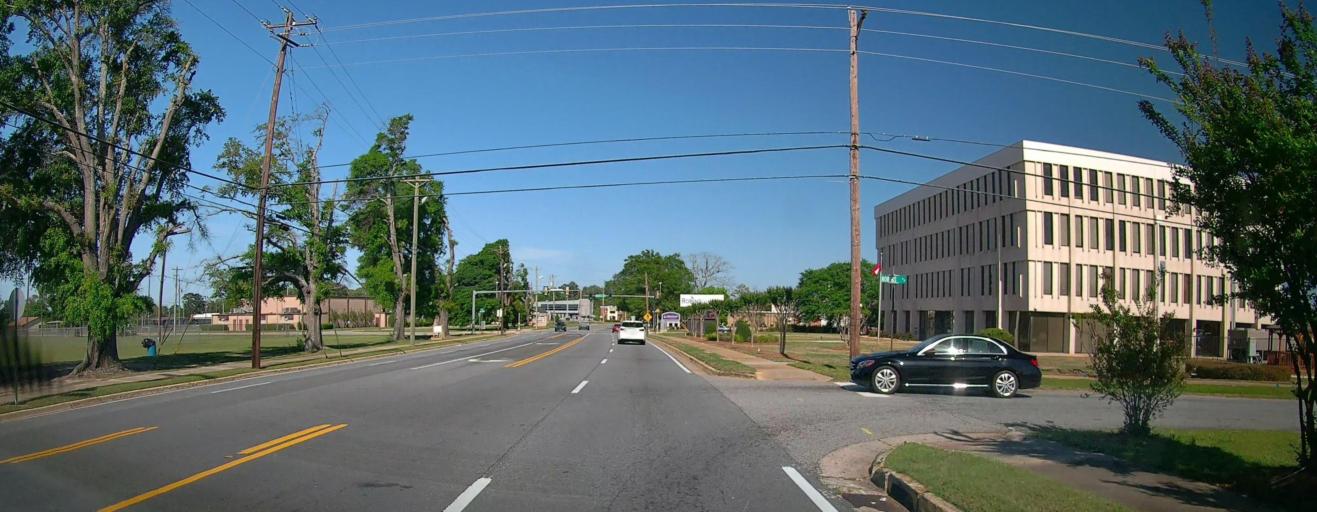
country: US
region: Georgia
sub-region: Houston County
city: Warner Robins
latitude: 32.6188
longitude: -83.6112
